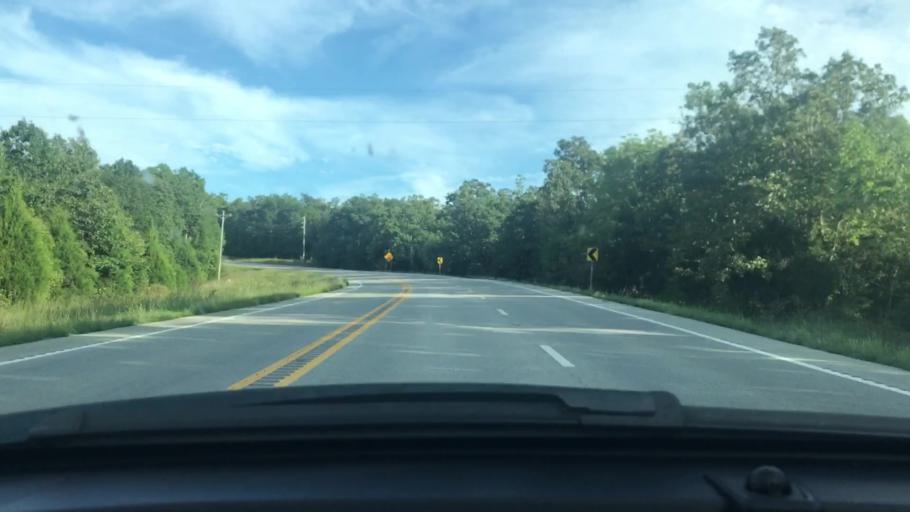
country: US
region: Arkansas
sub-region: Sharp County
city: Cherokee Village
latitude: 36.2750
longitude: -91.3224
